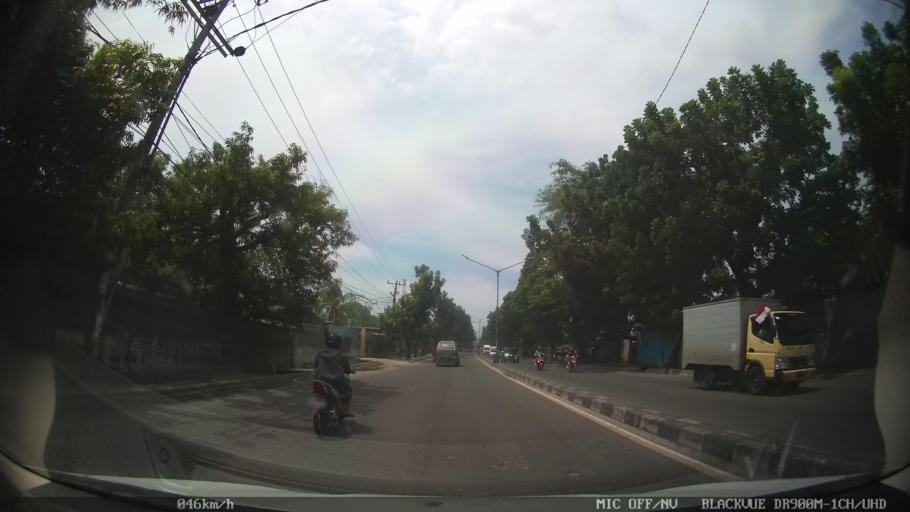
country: ID
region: North Sumatra
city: Medan
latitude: 3.6446
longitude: 98.6628
